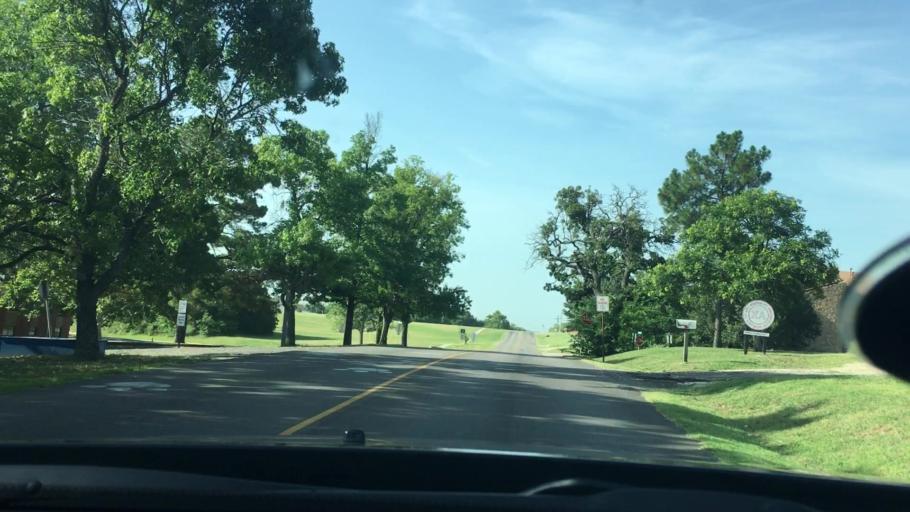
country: US
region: Oklahoma
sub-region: Pontotoc County
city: Ada
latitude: 34.7705
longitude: -96.6612
